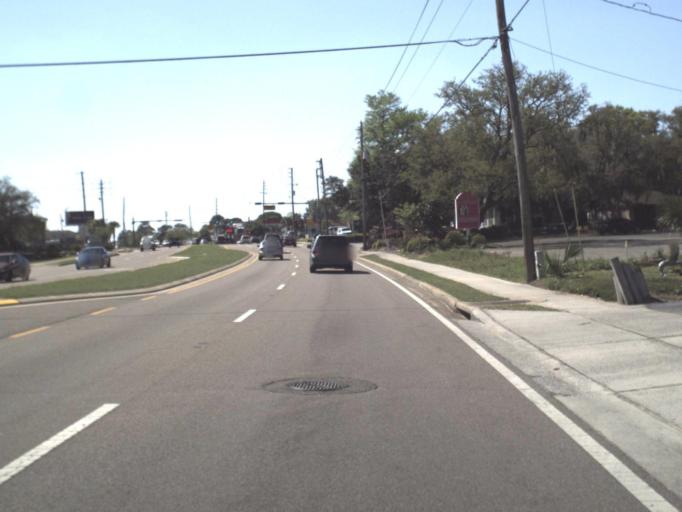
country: US
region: Florida
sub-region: Okaloosa County
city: Ocean City
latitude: 30.4484
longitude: -86.6120
